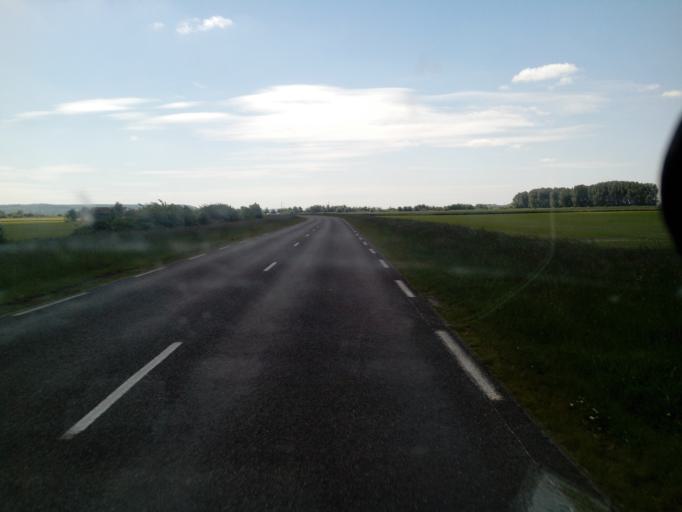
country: FR
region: Haute-Normandie
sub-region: Departement de la Seine-Maritime
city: Tancarville
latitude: 49.4502
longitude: 0.4342
